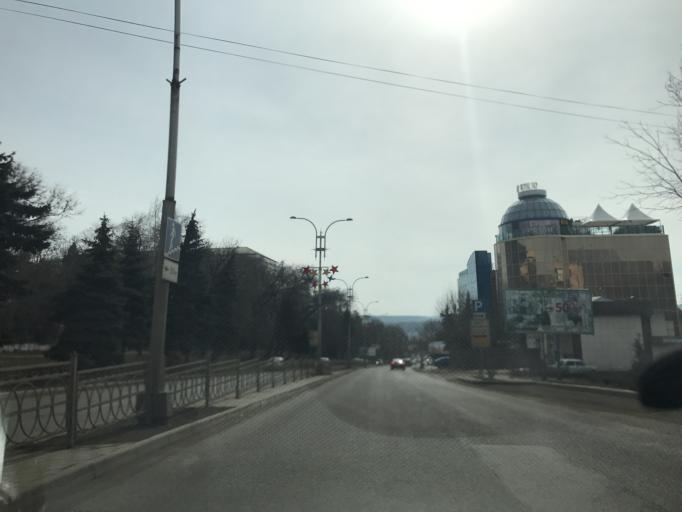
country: RU
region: Stavropol'skiy
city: Pyatigorsk
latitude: 44.0488
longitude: 43.0653
